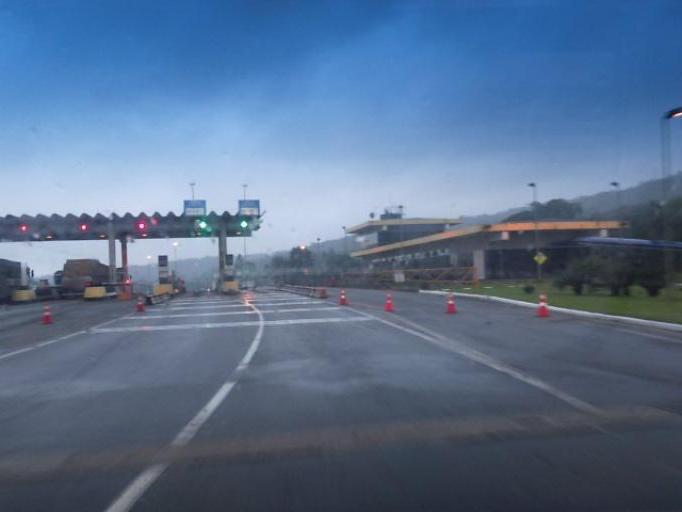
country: BR
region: Santa Catarina
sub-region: Joinville
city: Joinville
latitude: -25.9918
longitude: -48.8822
